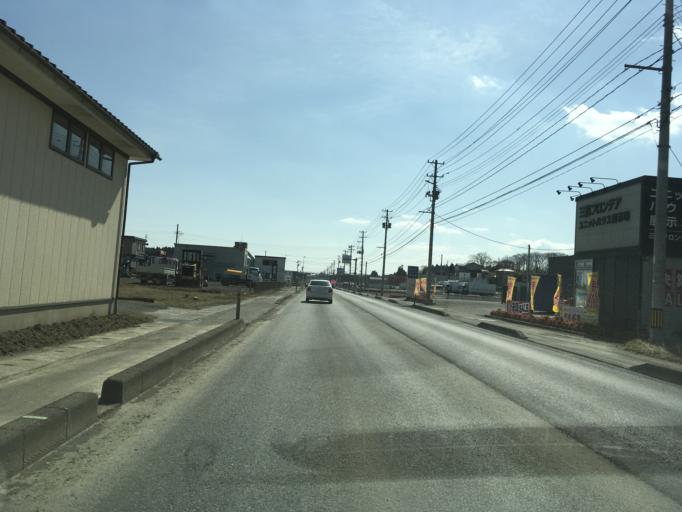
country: JP
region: Iwate
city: Ofunato
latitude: 38.8539
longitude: 141.5805
